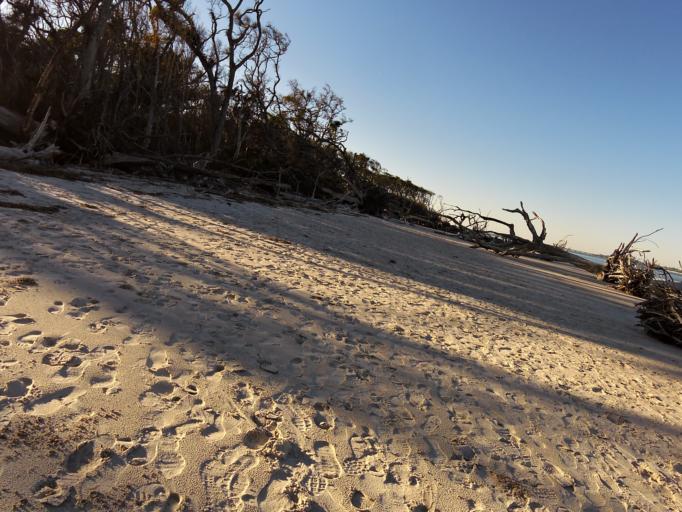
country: US
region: Florida
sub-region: Duval County
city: Atlantic Beach
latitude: 30.4942
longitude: -81.4387
